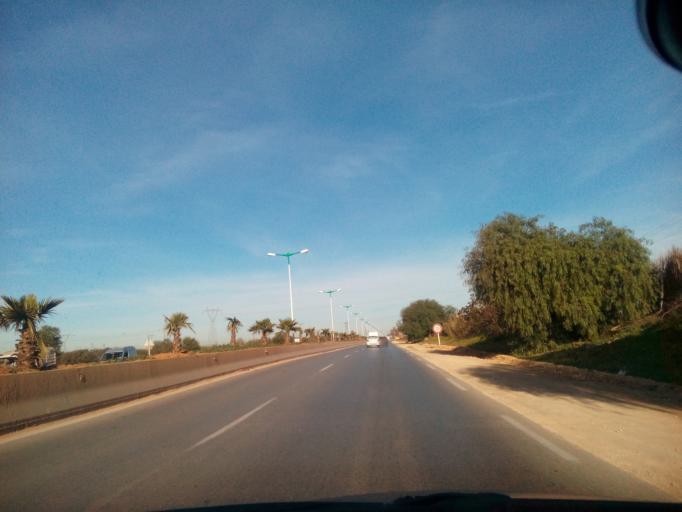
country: DZ
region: Mostaganem
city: Mostaganem
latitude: 35.8717
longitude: 0.1483
